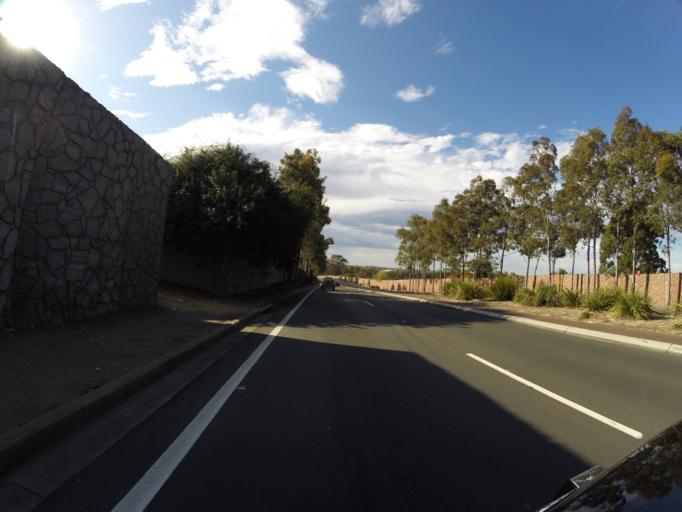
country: AU
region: New South Wales
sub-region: Fairfield
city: Cecil Park
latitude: -33.8769
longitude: 150.8681
